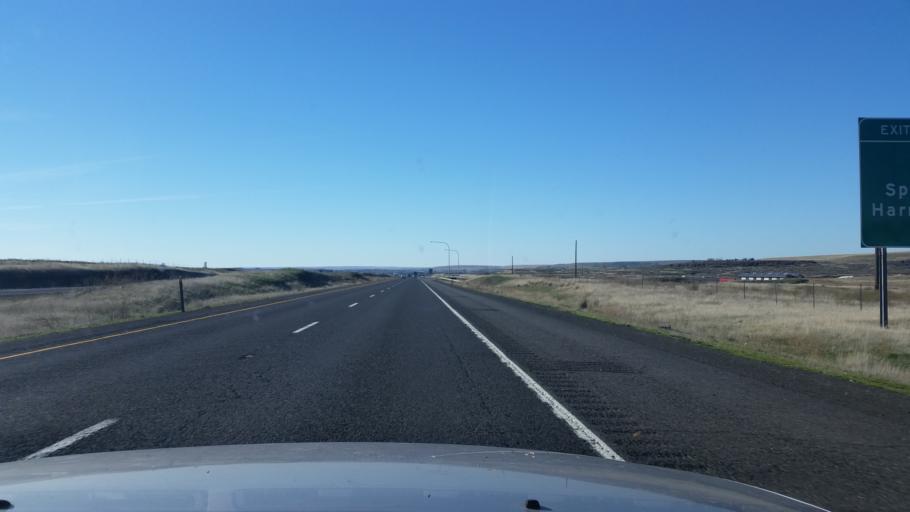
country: US
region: Washington
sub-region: Spokane County
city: Medical Lake
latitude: 47.3114
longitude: -117.9663
